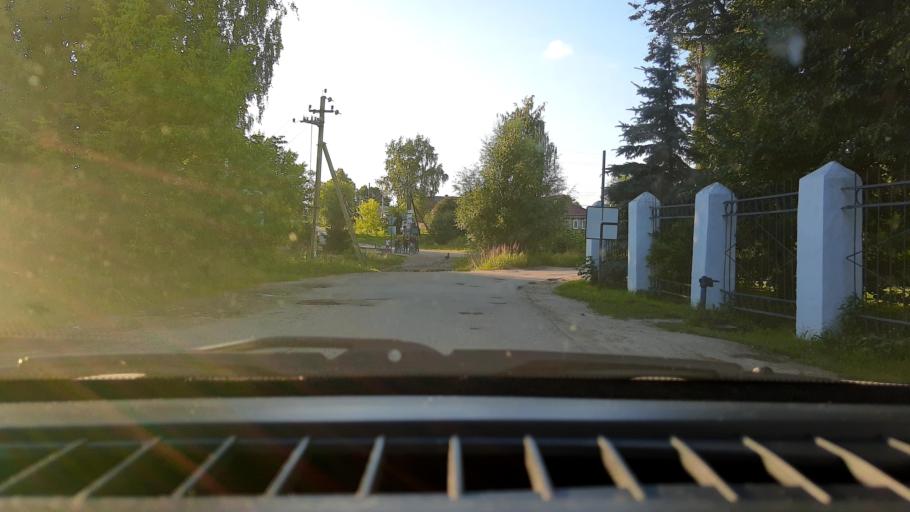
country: RU
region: Nizjnij Novgorod
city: Burevestnik
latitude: 56.1345
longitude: 43.9199
